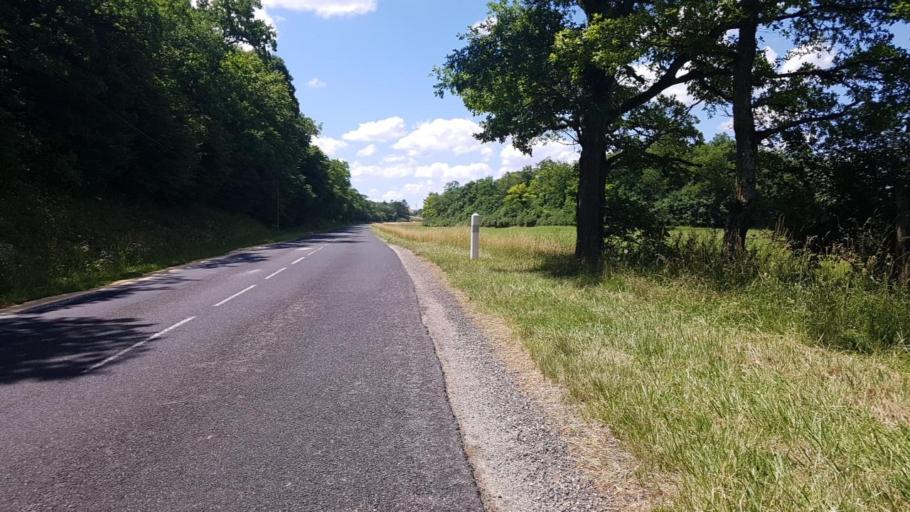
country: FR
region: Lorraine
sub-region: Departement de la Meuse
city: Vacon
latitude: 48.6703
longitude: 5.5579
